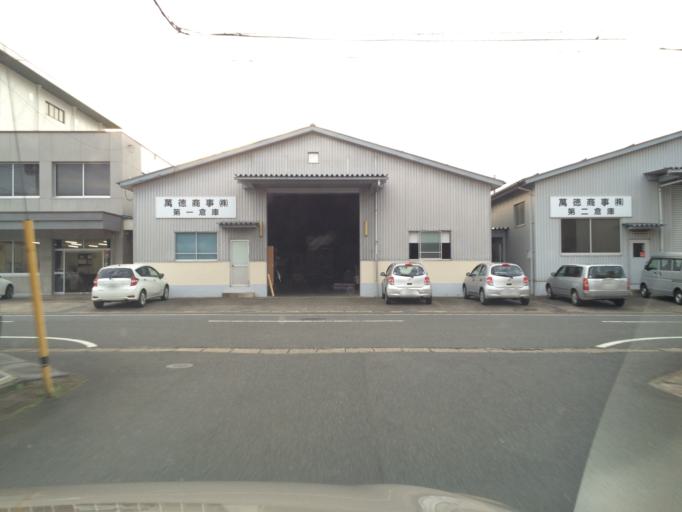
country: JP
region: Hyogo
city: Toyooka
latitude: 35.5148
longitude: 134.8199
